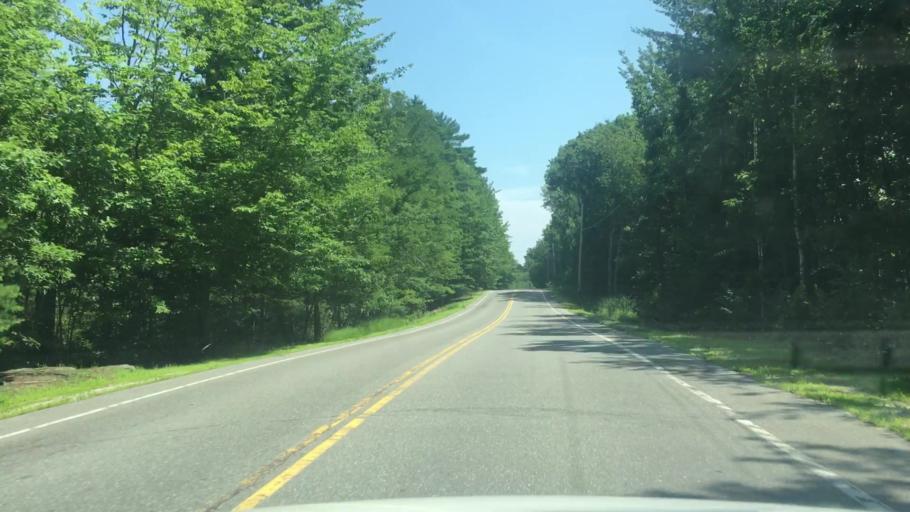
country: US
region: Maine
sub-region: Cumberland County
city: Falmouth
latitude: 43.7398
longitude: -70.2515
